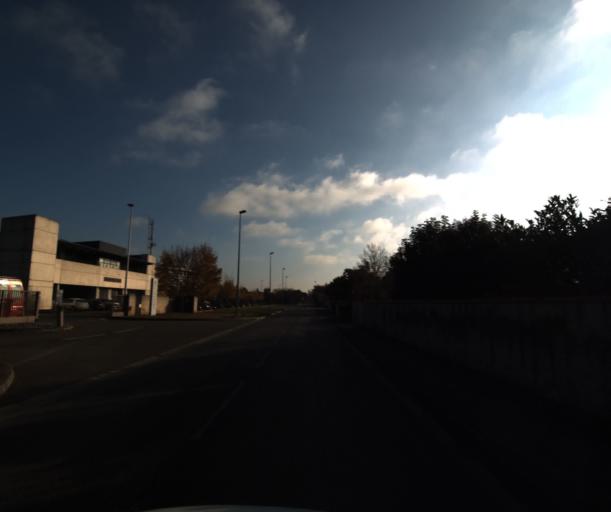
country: FR
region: Midi-Pyrenees
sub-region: Departement de la Haute-Garonne
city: Colomiers
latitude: 43.5929
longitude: 1.3571
